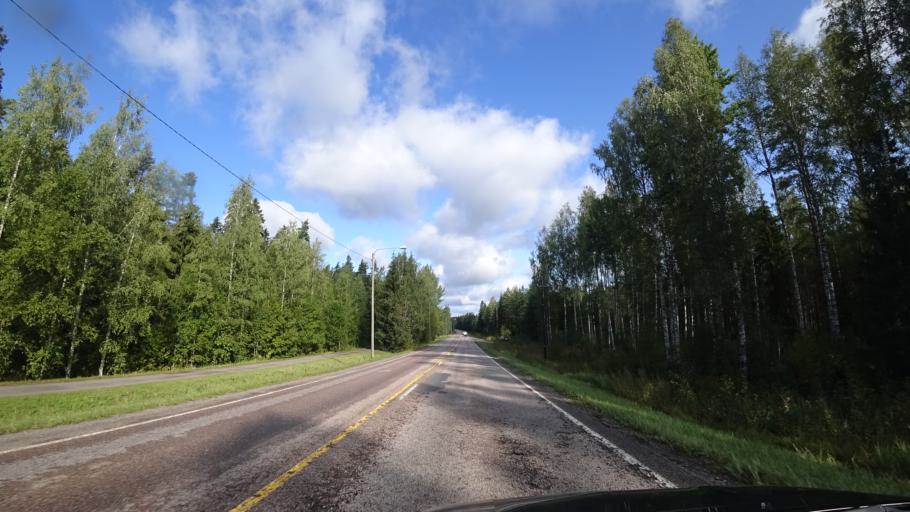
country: FI
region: Uusimaa
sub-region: Helsinki
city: Tuusula
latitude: 60.4249
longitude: 24.9975
